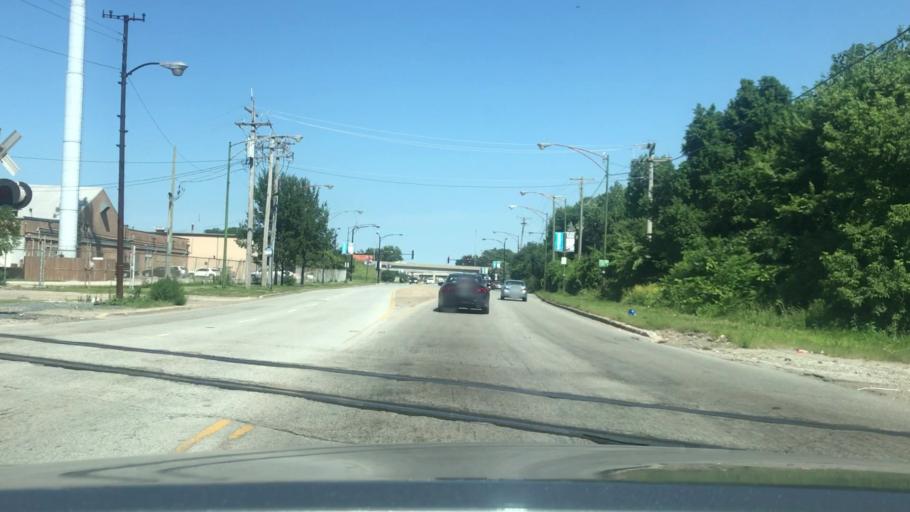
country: US
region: Illinois
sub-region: Cook County
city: Dolton
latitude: 41.7076
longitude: -87.5964
